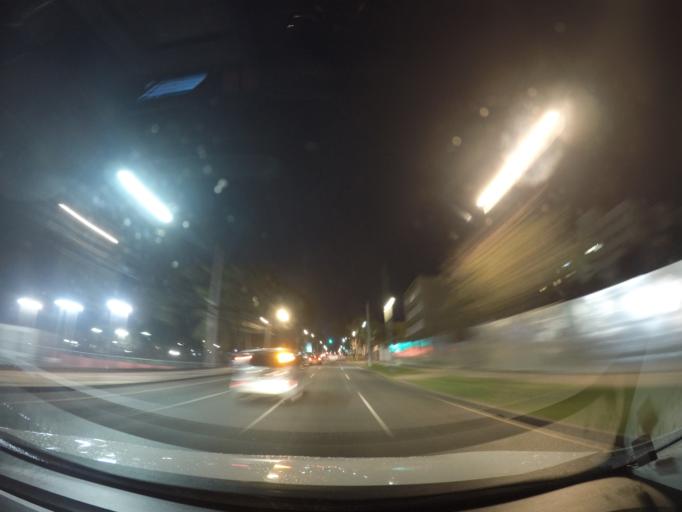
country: BR
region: Parana
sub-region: Curitiba
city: Curitiba
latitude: -25.4470
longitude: -49.2739
